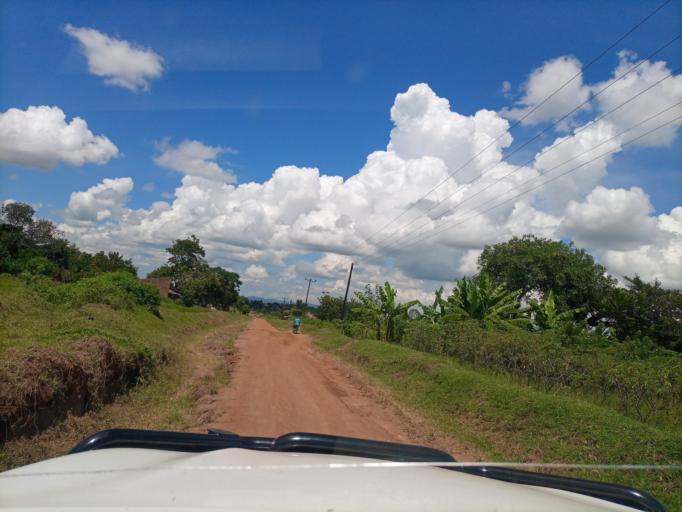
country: UG
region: Eastern Region
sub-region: Tororo District
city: Tororo
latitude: 0.6866
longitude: 34.0088
